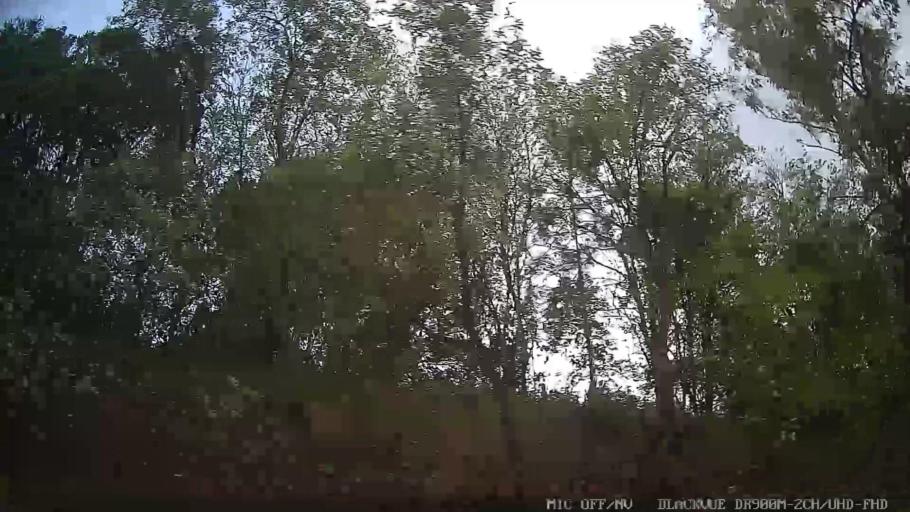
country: BR
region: Sao Paulo
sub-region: Itatiba
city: Itatiba
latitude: -22.9201
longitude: -46.7837
